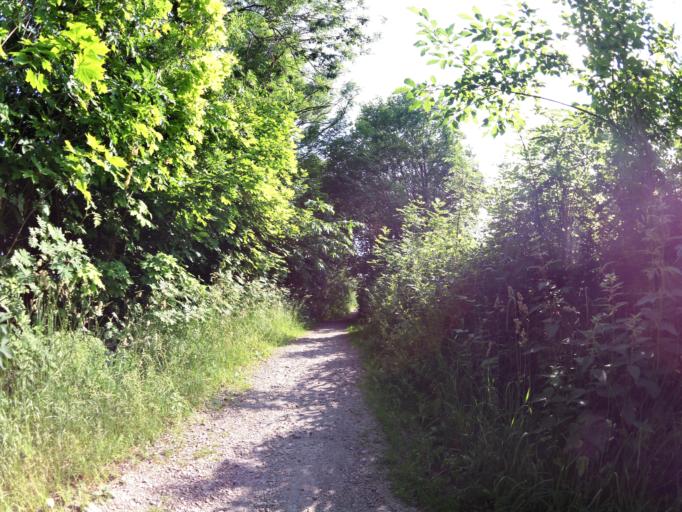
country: NO
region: Ostfold
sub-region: Fredrikstad
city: Fredrikstad
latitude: 59.2526
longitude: 11.0142
